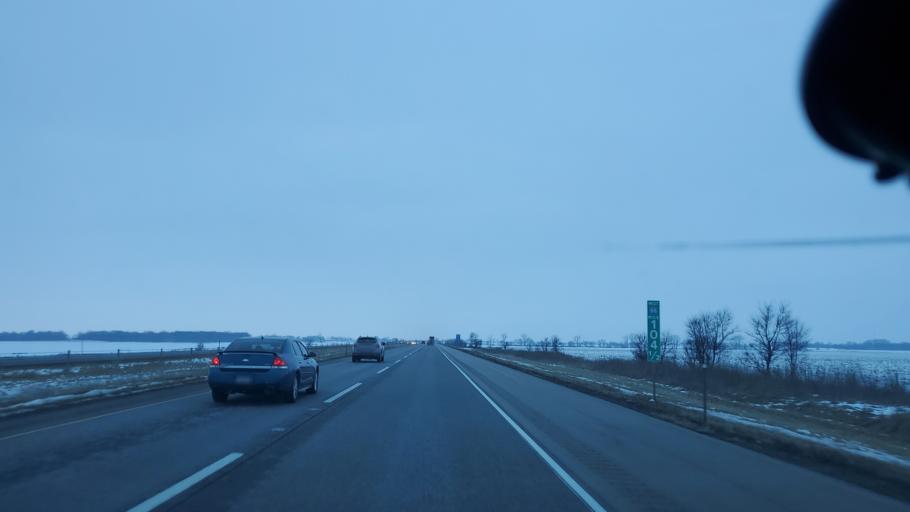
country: US
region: Illinois
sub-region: Kane County
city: Elburn
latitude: 41.8591
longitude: -88.5374
